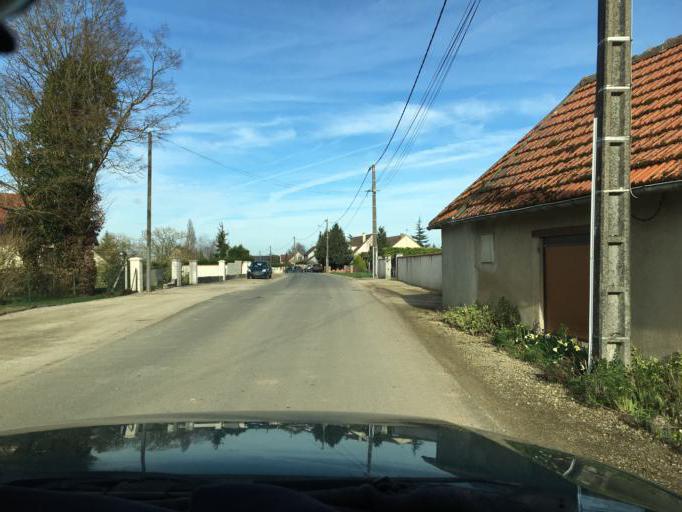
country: FR
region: Centre
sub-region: Departement du Loiret
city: Beaugency
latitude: 47.7840
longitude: 1.6054
